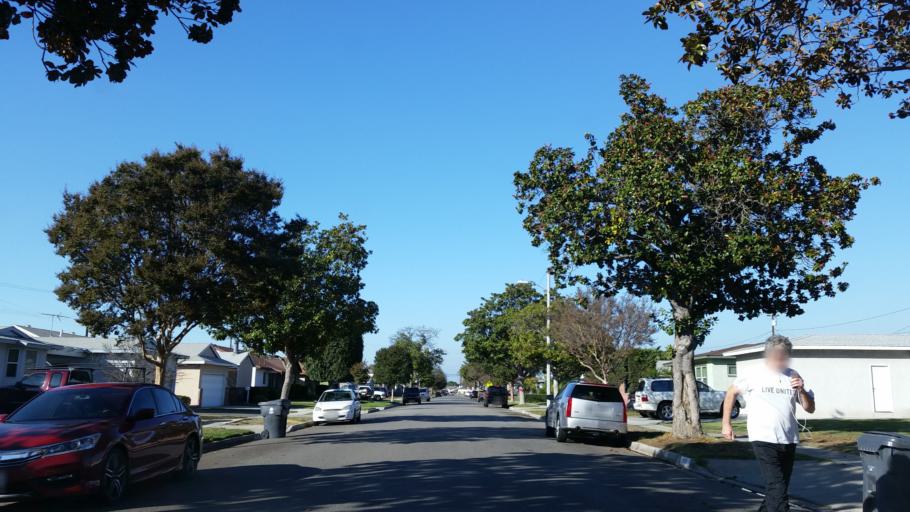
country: US
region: California
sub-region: Los Angeles County
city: Lakewood
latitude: 33.8588
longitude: -118.1111
